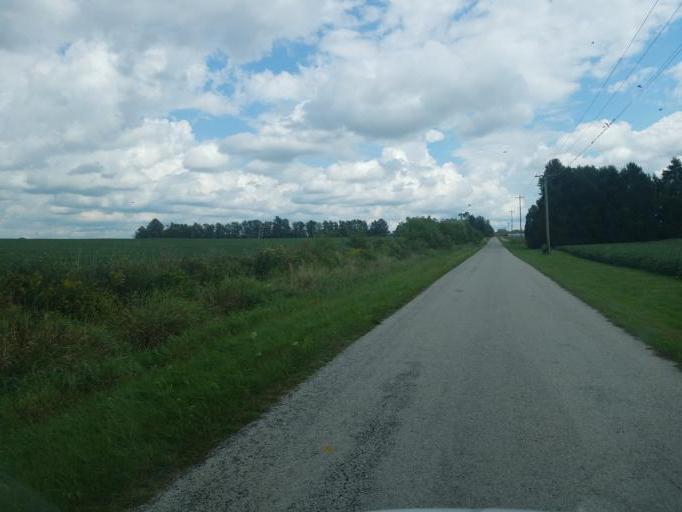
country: US
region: Ohio
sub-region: Huron County
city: Plymouth
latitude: 41.0454
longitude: -82.6312
